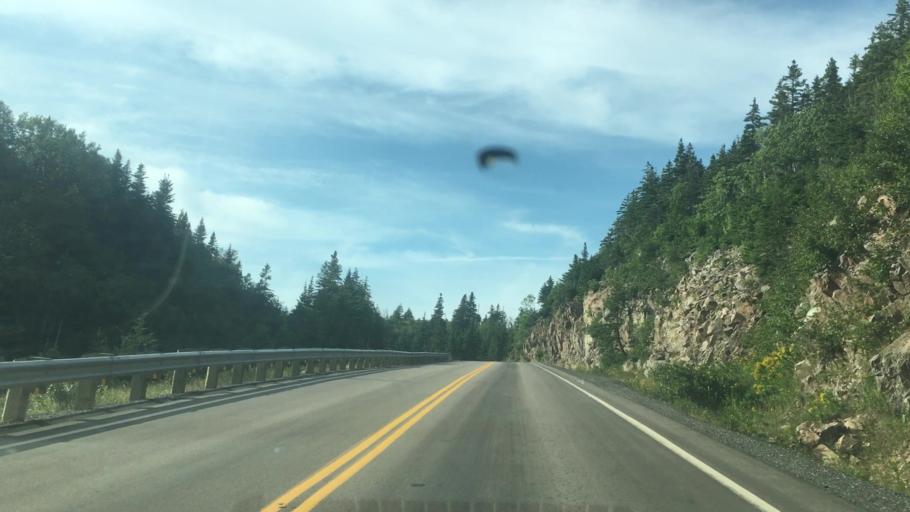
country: CA
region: Nova Scotia
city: Sydney Mines
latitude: 46.8226
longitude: -60.6549
